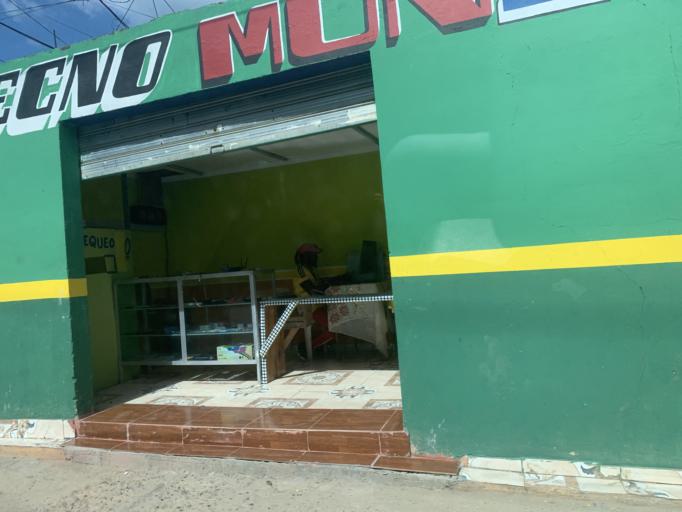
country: DO
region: Monte Plata
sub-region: Yamasa
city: Yamasa
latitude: 18.7731
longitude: -70.0224
